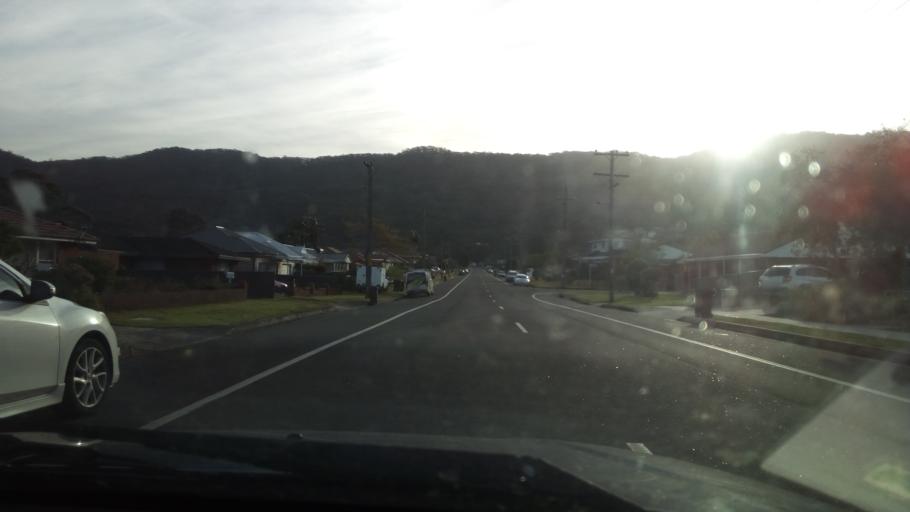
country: AU
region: New South Wales
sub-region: Wollongong
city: Mount Ousley
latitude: -34.3846
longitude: 150.8803
